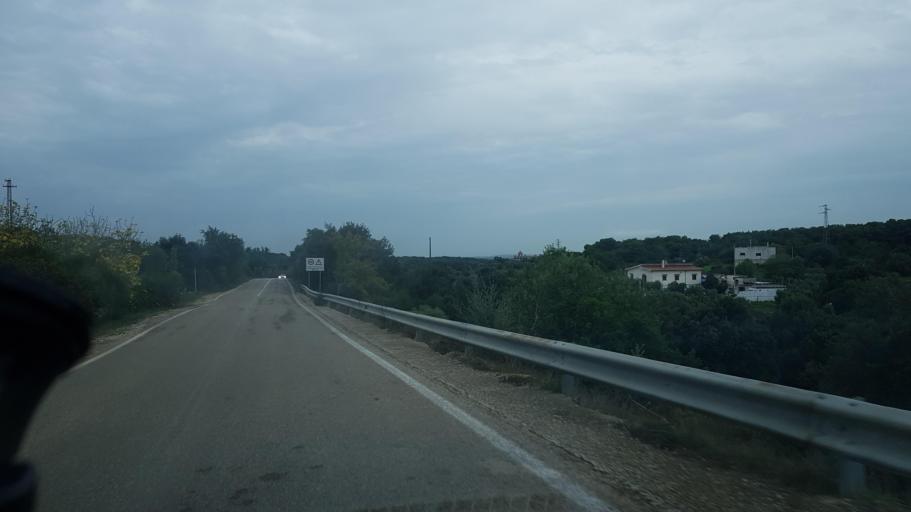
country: IT
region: Apulia
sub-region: Provincia di Brindisi
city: Ostuni
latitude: 40.7380
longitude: 17.5410
